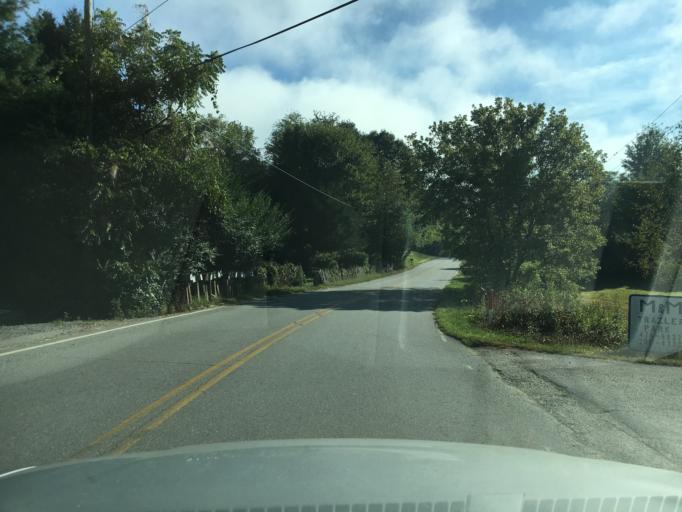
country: US
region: North Carolina
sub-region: Haywood County
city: Lake Junaluska
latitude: 35.5312
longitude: -82.9376
